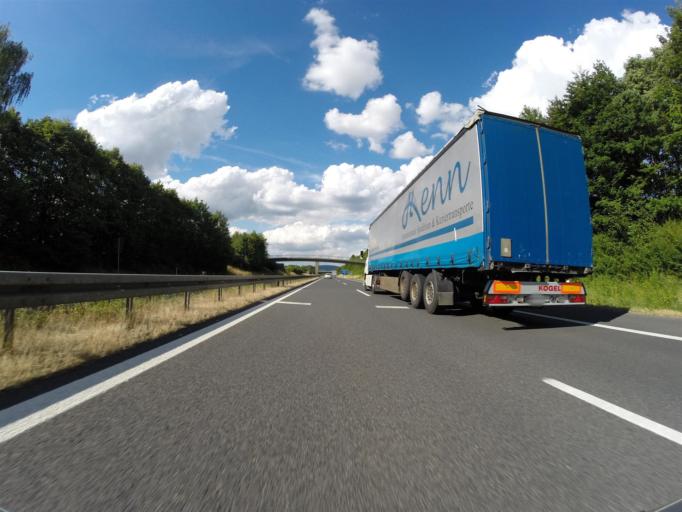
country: DE
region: Bavaria
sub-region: Upper Franconia
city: Bad Staffelstein
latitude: 50.1047
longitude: 11.0115
